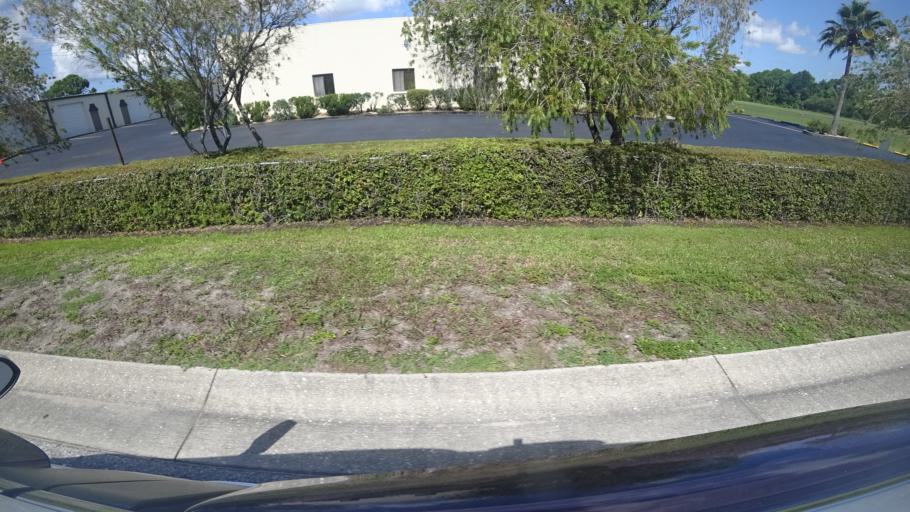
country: US
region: Florida
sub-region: Manatee County
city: Whitfield
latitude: 27.4300
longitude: -82.5343
